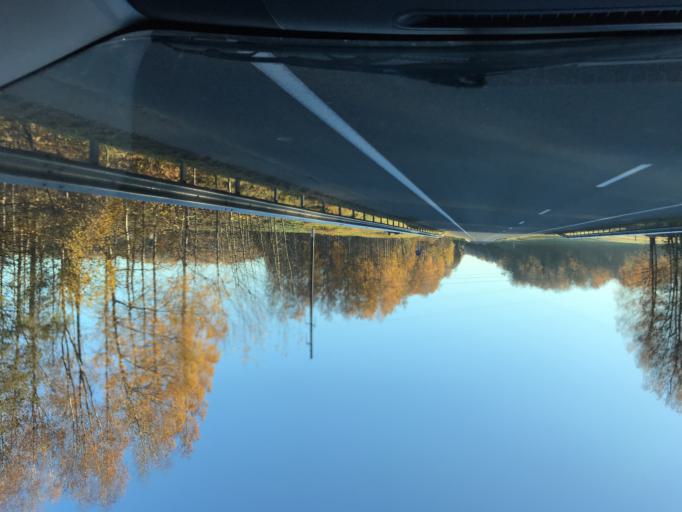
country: BY
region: Vitebsk
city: Vitebsk
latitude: 55.0414
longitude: 30.3166
